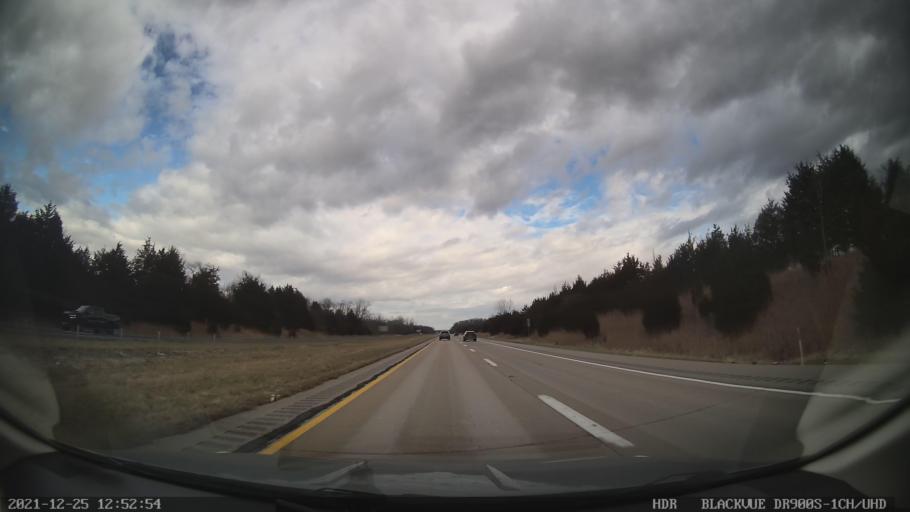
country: US
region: Maryland
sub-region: Frederick County
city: Emmitsburg
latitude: 39.7477
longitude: -77.2734
